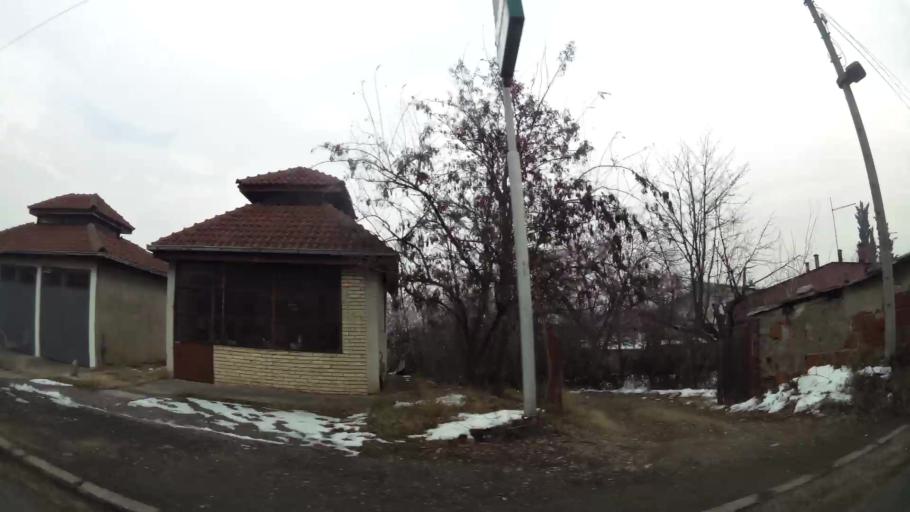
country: MK
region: Cair
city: Cair
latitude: 42.0167
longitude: 21.4565
